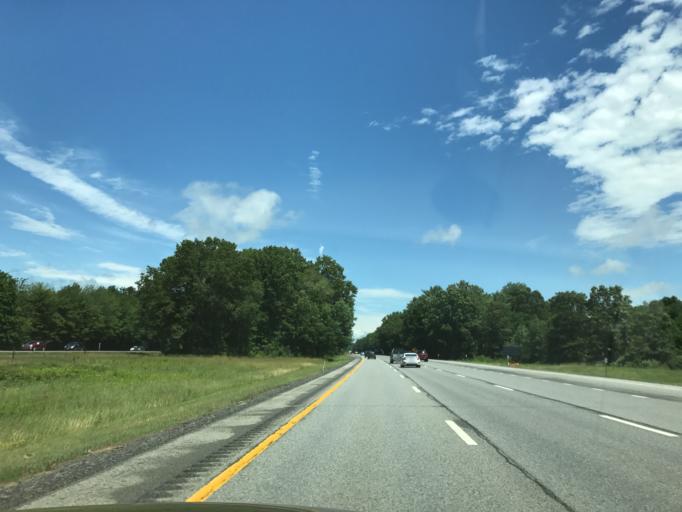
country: US
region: New York
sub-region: Saratoga County
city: Saratoga Springs
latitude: 43.1727
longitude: -73.7105
